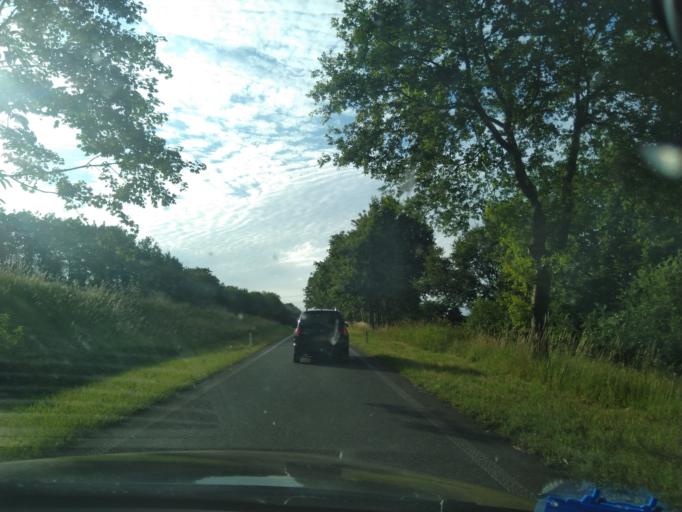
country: NL
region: Groningen
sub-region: Gemeente  Oldambt
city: Winschoten
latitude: 53.1020
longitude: 7.0724
